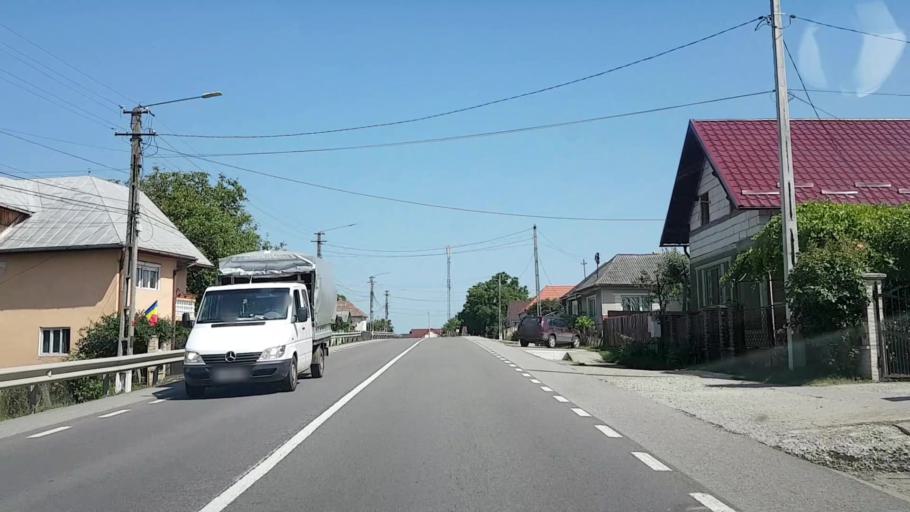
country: RO
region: Bistrita-Nasaud
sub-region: Comuna Uriu
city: Cristestii Ciceului
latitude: 47.1902
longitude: 24.1015
